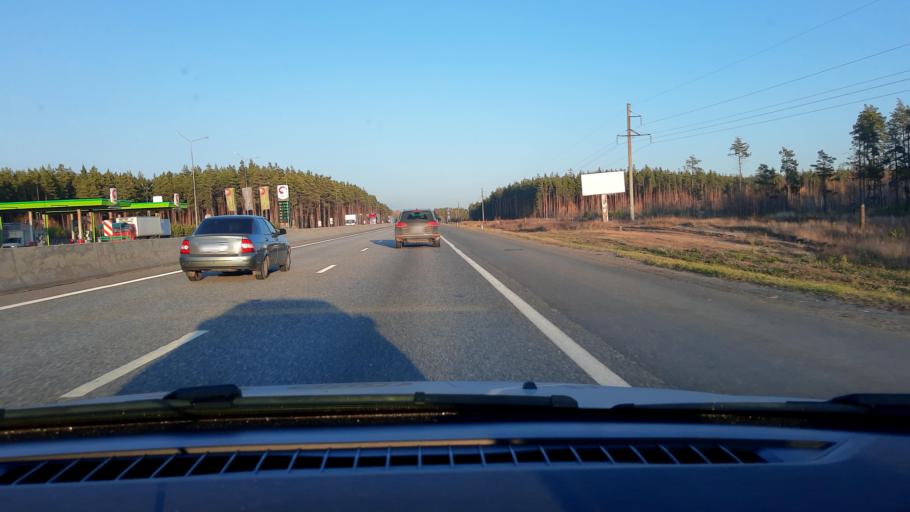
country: RU
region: Nizjnij Novgorod
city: Mulino
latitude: 56.2609
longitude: 42.9161
